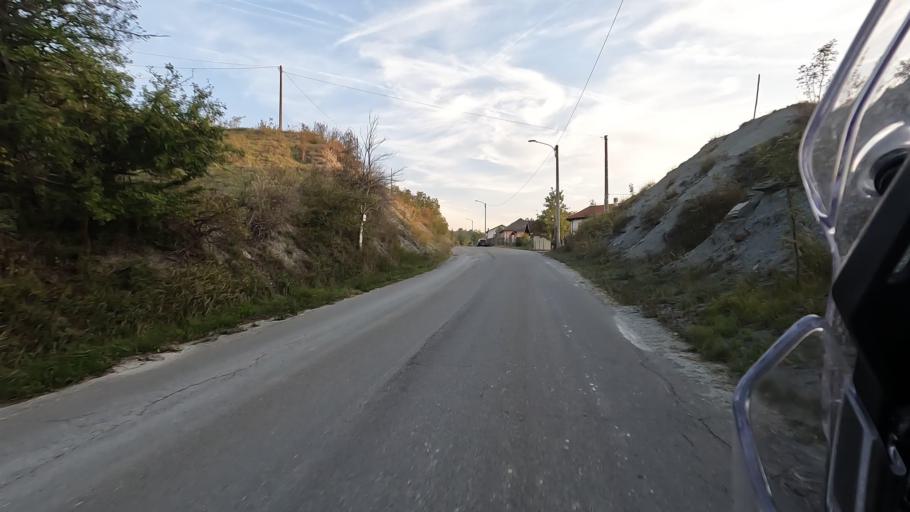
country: IT
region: Liguria
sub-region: Provincia di Savona
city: Mioglia
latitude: 44.4817
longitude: 8.4133
